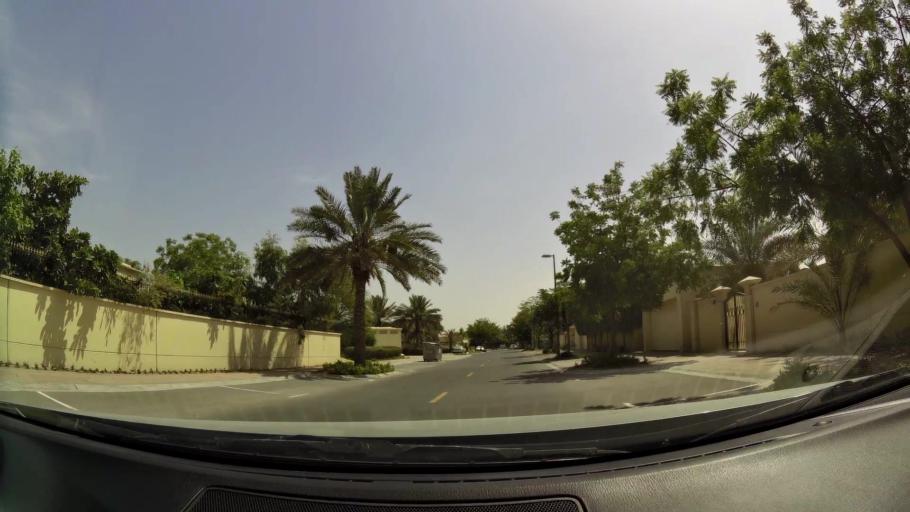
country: AE
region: Ash Shariqah
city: Sharjah
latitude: 25.1827
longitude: 55.4418
